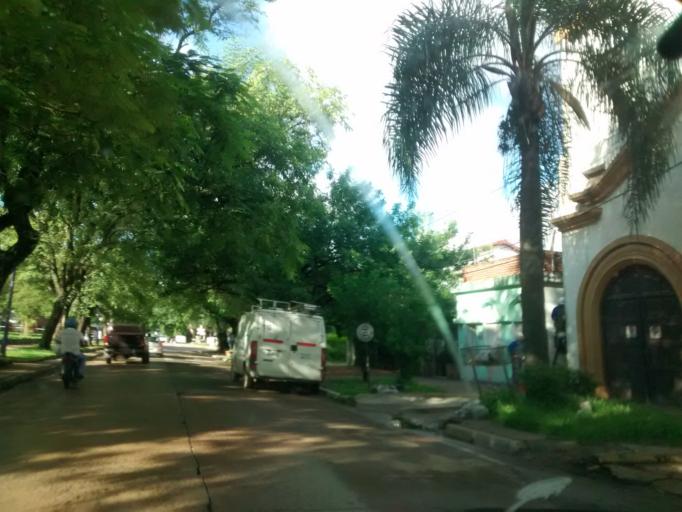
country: AR
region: Chaco
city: Resistencia
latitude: -27.4575
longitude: -58.9867
